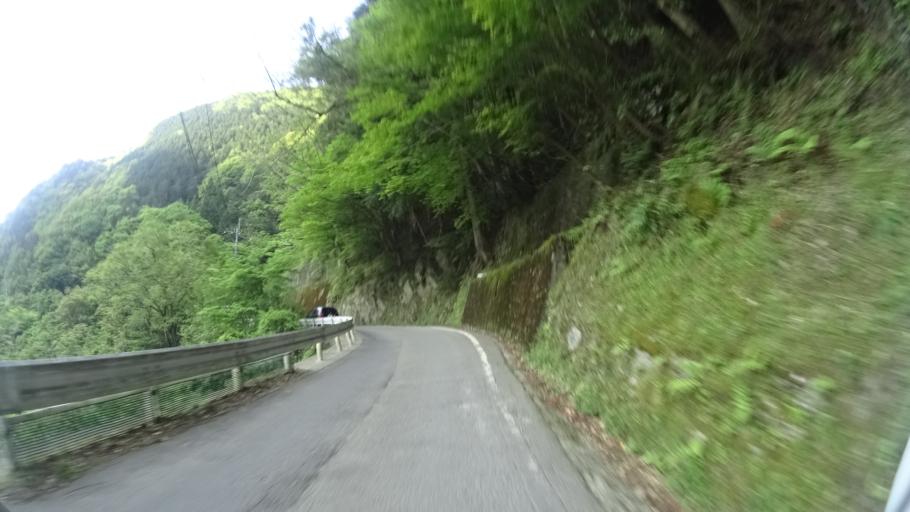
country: JP
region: Tokushima
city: Ikedacho
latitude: 33.8999
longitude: 133.8155
